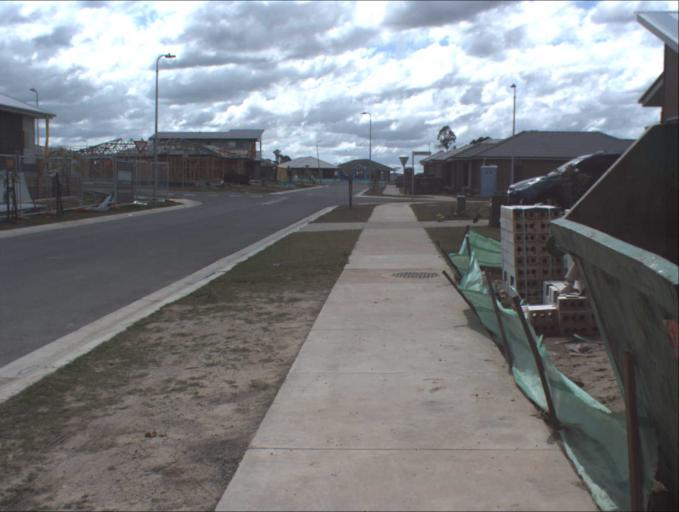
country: AU
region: Queensland
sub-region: Logan
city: Chambers Flat
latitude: -27.8100
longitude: 153.1133
